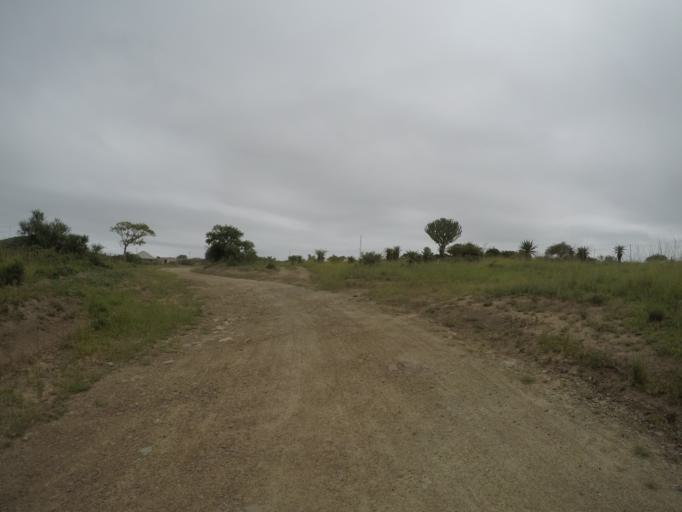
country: ZA
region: KwaZulu-Natal
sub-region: uThungulu District Municipality
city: Empangeni
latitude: -28.6093
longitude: 31.8370
